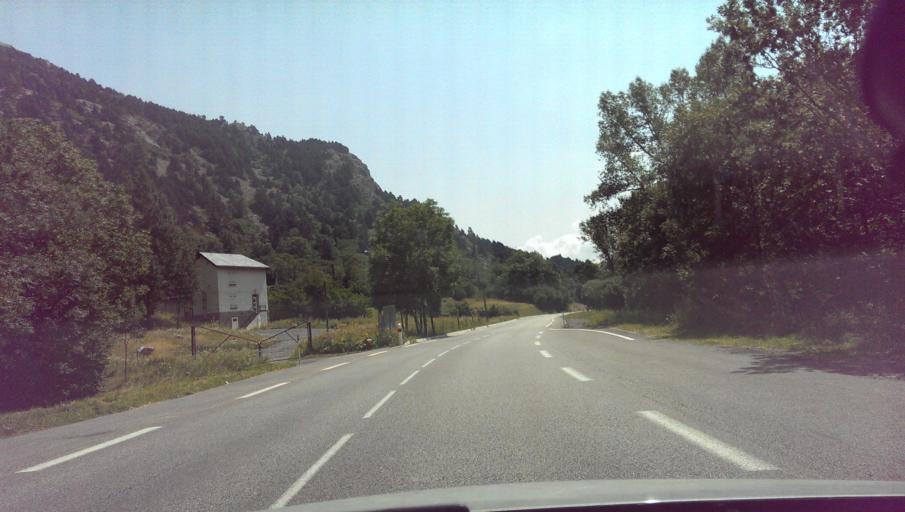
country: ES
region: Catalonia
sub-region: Provincia de Girona
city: Meranges
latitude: 42.5097
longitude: 1.8303
